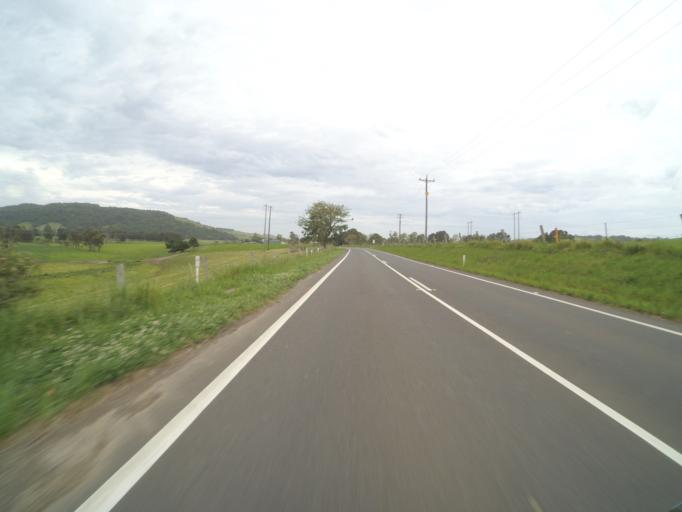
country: AU
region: New South Wales
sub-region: Kiama
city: Jamberoo
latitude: -34.6489
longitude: 150.7862
